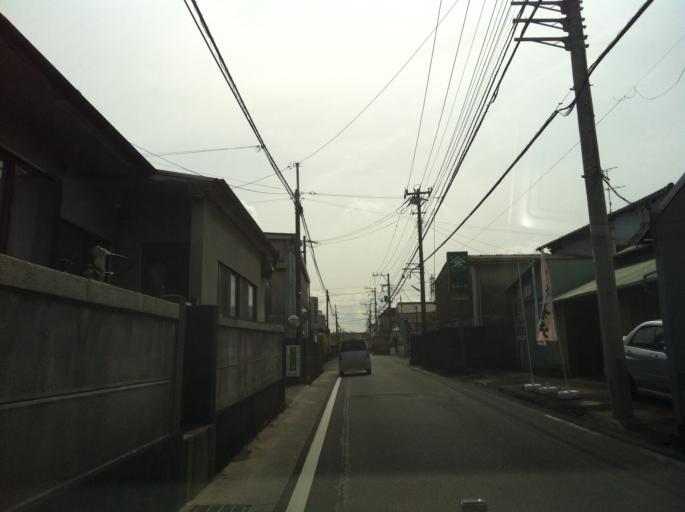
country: JP
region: Shizuoka
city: Numazu
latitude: 35.1378
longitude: 138.8112
